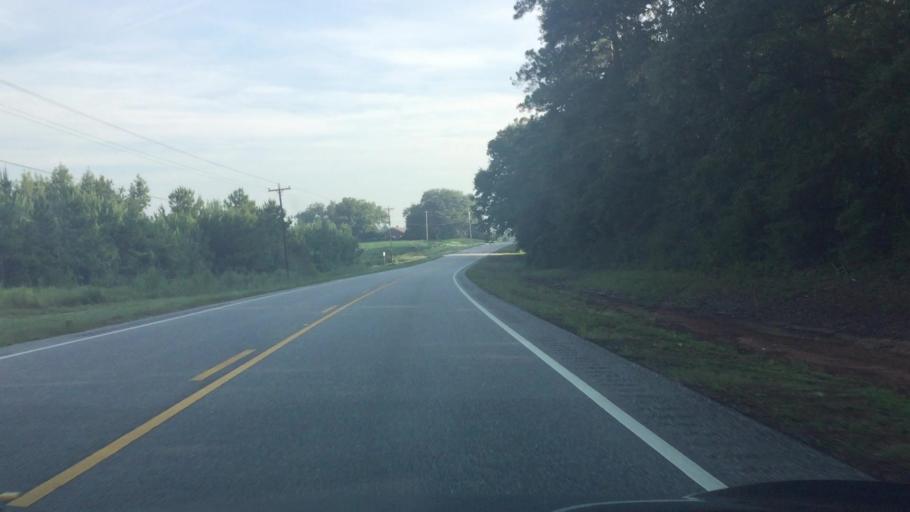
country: US
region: Alabama
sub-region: Covington County
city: Andalusia
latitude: 31.1668
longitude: -86.4601
